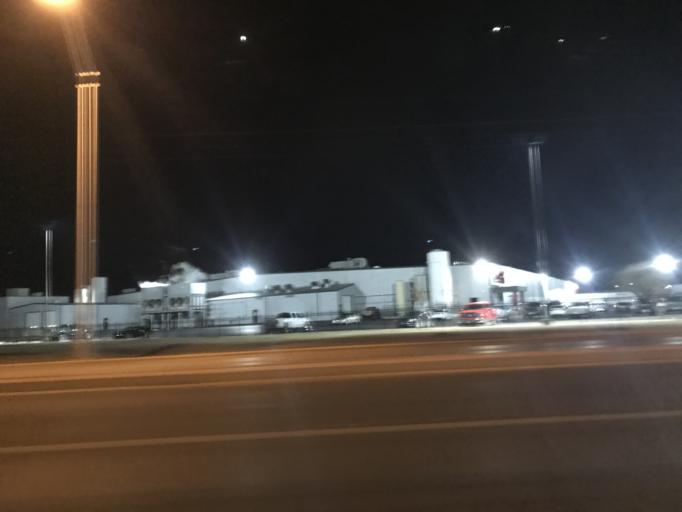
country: US
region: Texas
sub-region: Taylor County
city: Abilene
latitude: 32.4805
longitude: -99.6934
